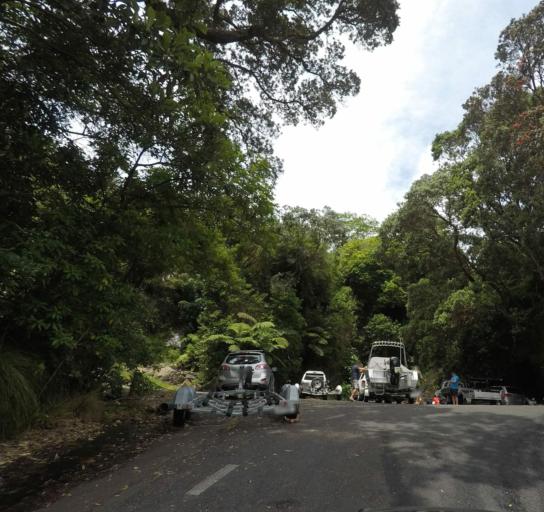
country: NZ
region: Auckland
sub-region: Auckland
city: Warkworth
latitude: -36.2891
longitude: 174.8069
